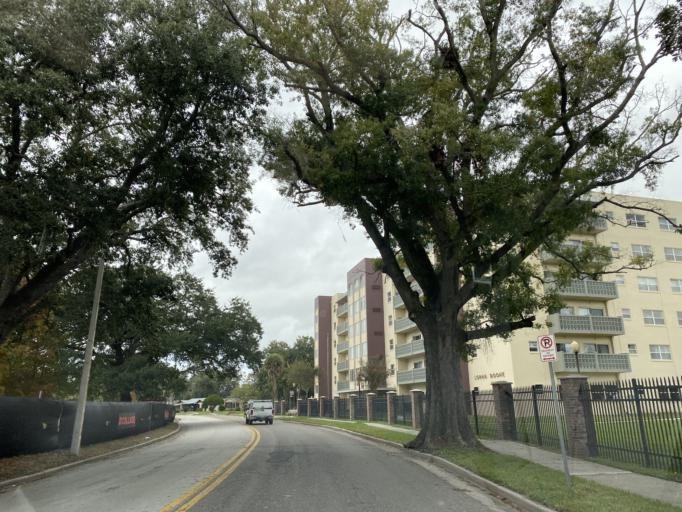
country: US
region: Florida
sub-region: Orange County
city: Orlando
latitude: 28.5424
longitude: -81.4018
